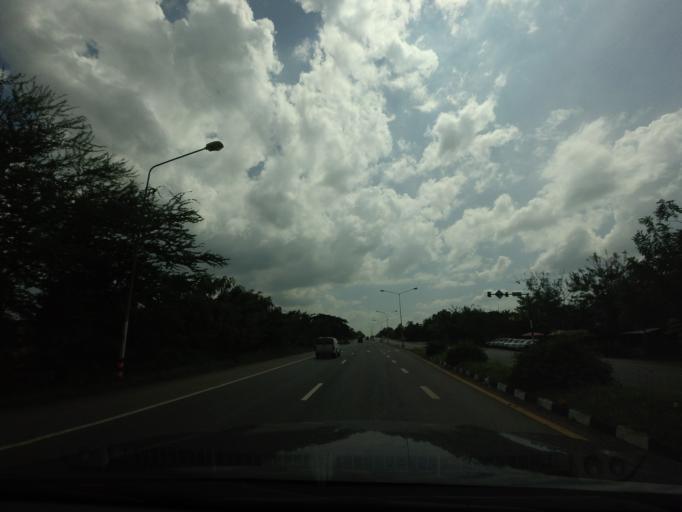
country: TH
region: Phetchabun
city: Phetchabun
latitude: 16.2227
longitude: 101.0891
